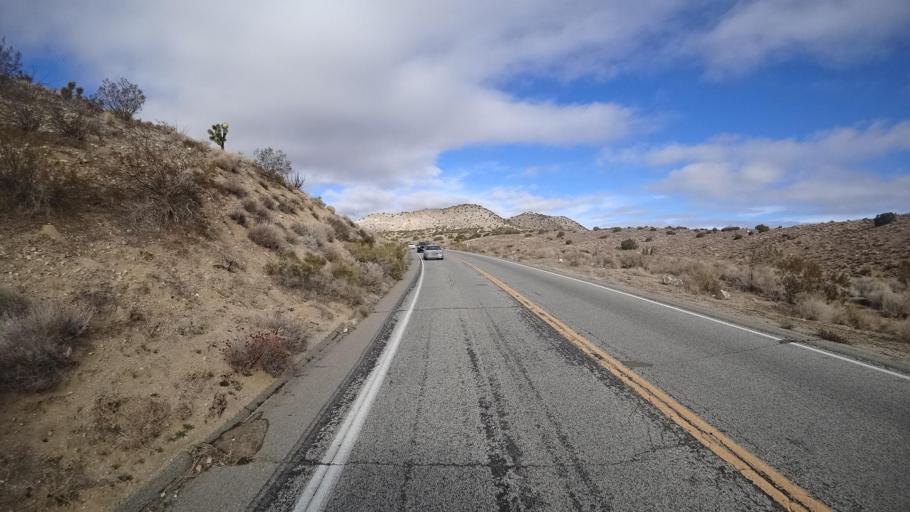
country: US
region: California
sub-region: Kern County
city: Tehachapi
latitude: 35.0094
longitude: -118.3408
